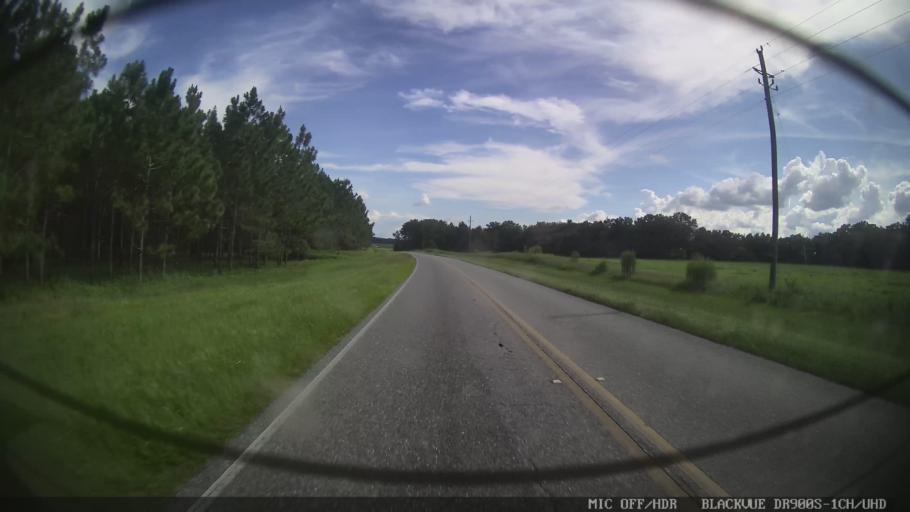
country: US
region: Georgia
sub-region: Echols County
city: Statenville
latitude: 30.5994
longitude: -83.2238
